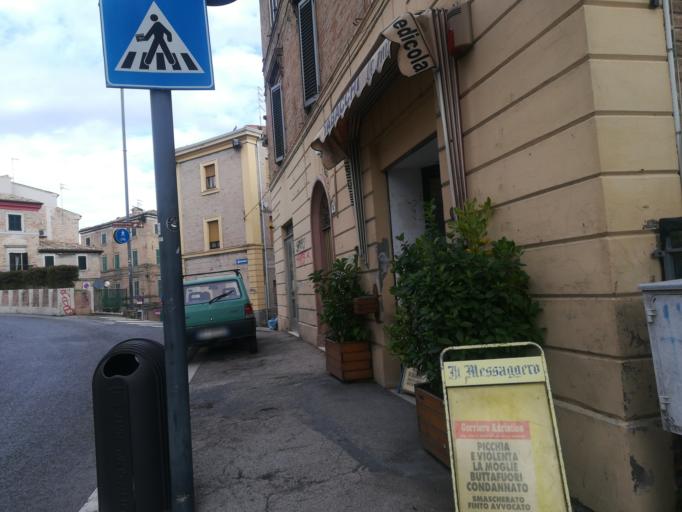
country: IT
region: The Marches
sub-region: Provincia di Macerata
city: Macerata
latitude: 43.3007
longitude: 13.4578
